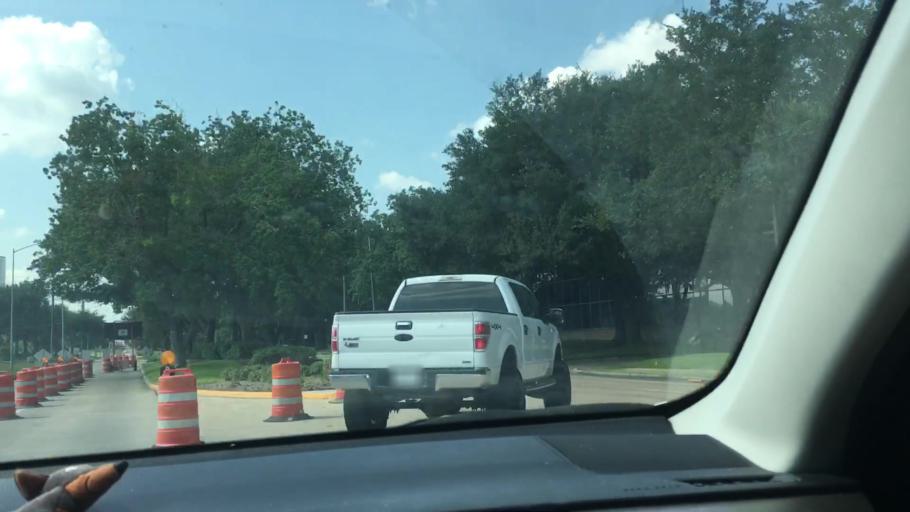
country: US
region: Texas
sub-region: Harris County
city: Bunker Hill Village
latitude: 29.7306
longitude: -95.5717
